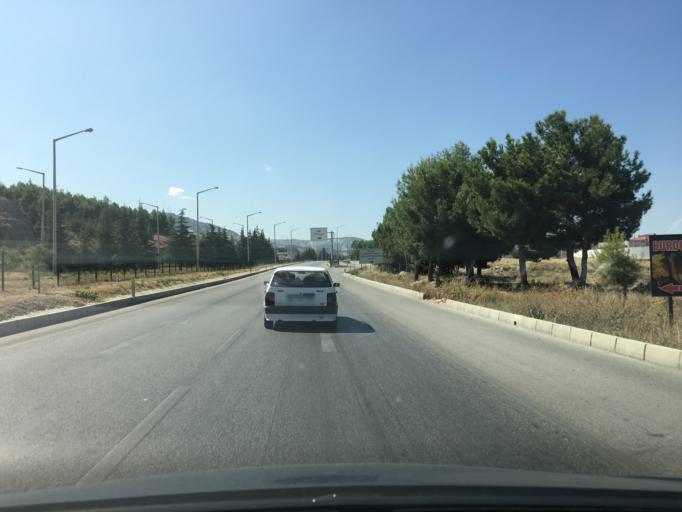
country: TR
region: Burdur
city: Burdur
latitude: 37.7397
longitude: 30.3121
